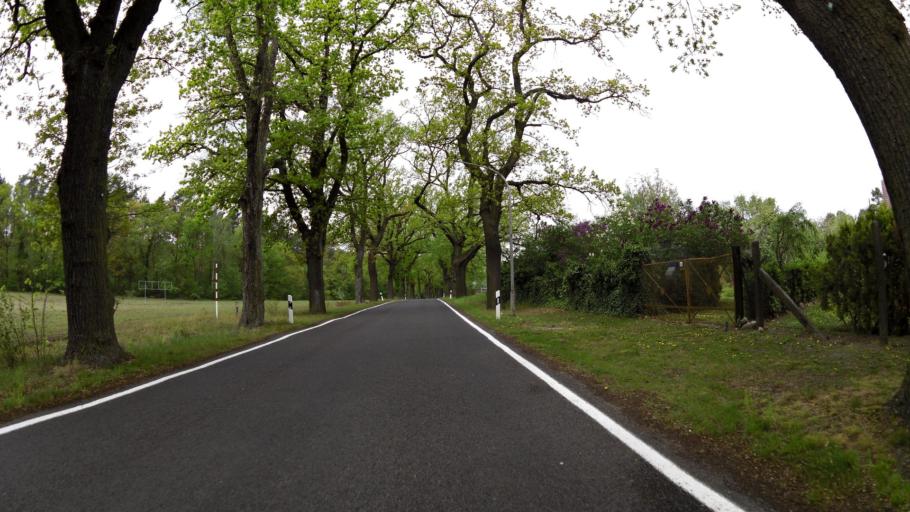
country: DE
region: Brandenburg
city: Mittenwalde
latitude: 52.2056
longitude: 13.5674
